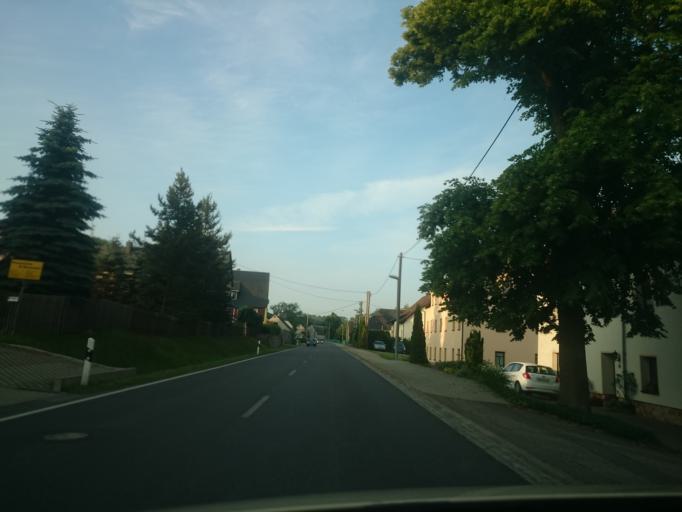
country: DE
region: Saxony
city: Grosshartmannsdorf
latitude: 50.7921
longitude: 13.3186
